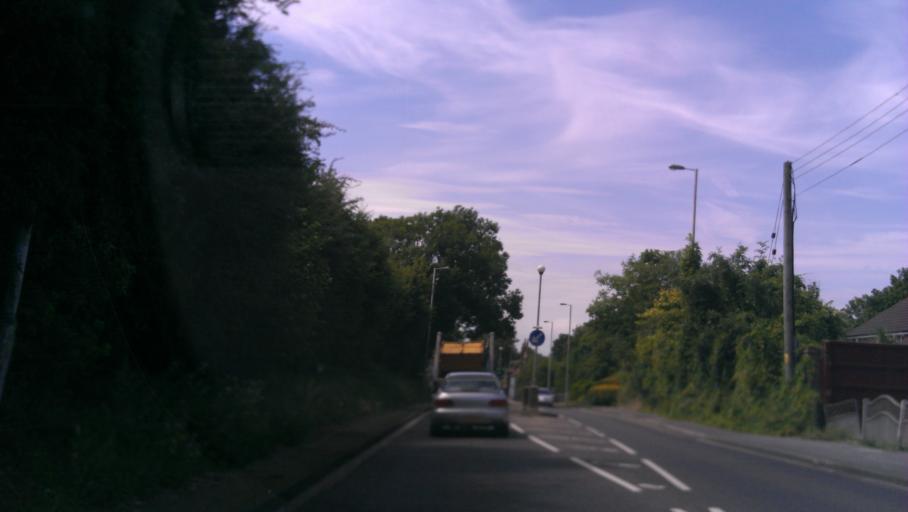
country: GB
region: England
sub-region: Kent
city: Faversham
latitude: 51.3072
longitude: 0.8963
